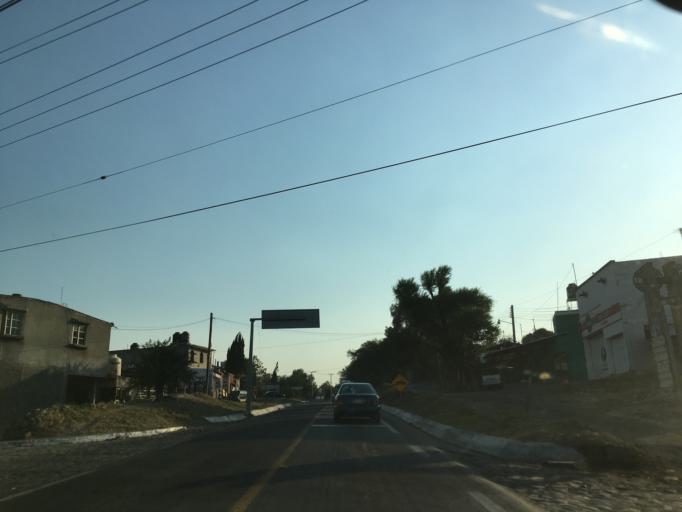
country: MX
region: Michoacan
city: Charo
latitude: 19.7523
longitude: -101.0467
